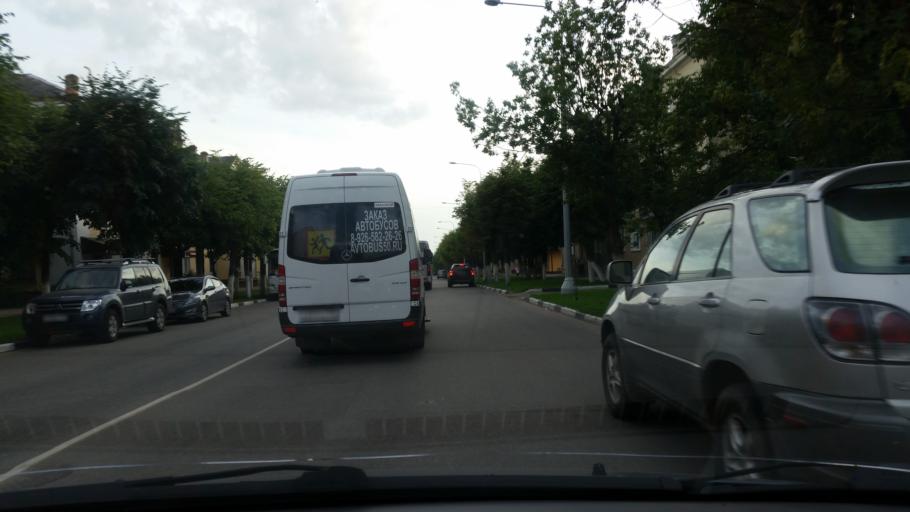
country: RU
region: Moskovskaya
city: Serpukhov
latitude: 54.9224
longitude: 37.4293
